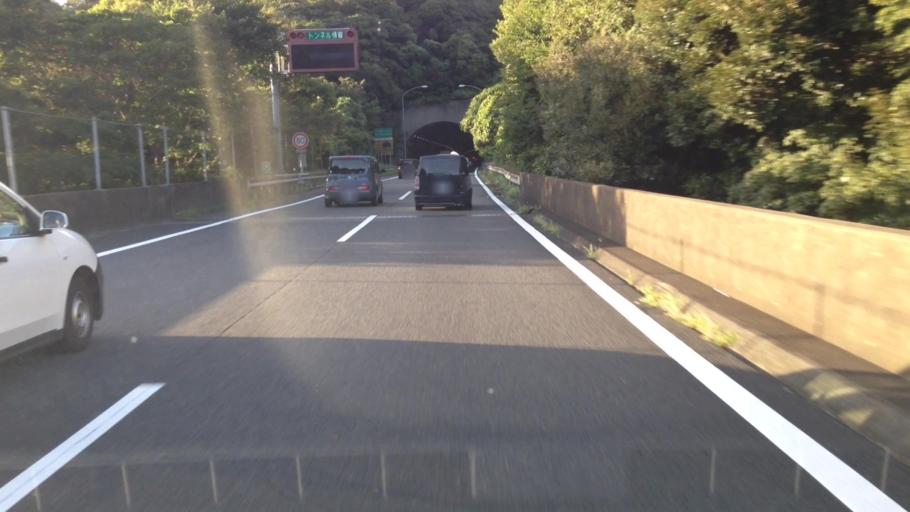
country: JP
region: Kanagawa
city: Zushi
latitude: 35.3103
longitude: 139.6073
